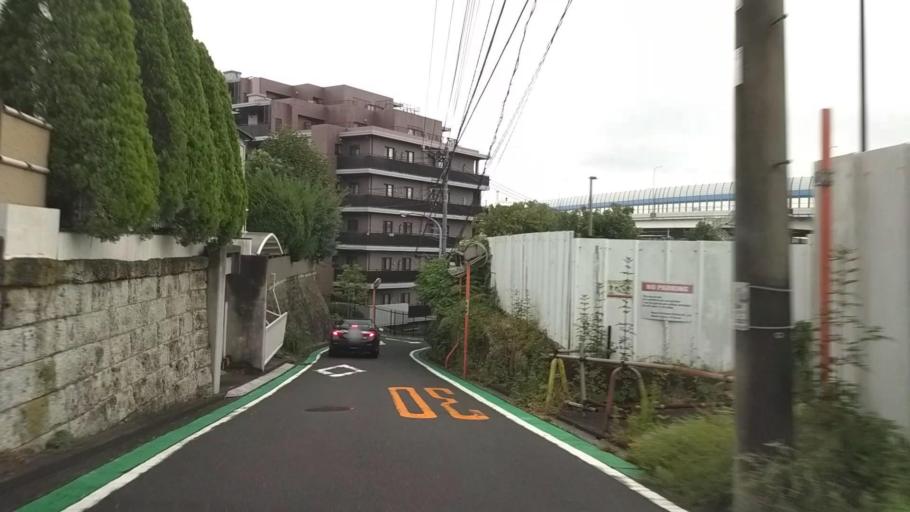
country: JP
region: Kanagawa
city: Yokohama
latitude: 35.4195
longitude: 139.6494
